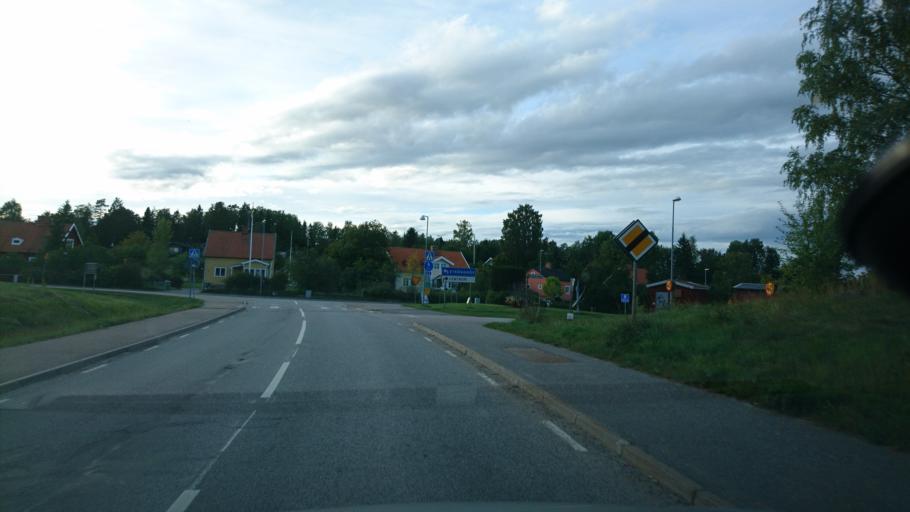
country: SE
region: Soedermanland
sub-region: Strangnas Kommun
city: Stallarholmen
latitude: 59.3568
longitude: 17.2065
